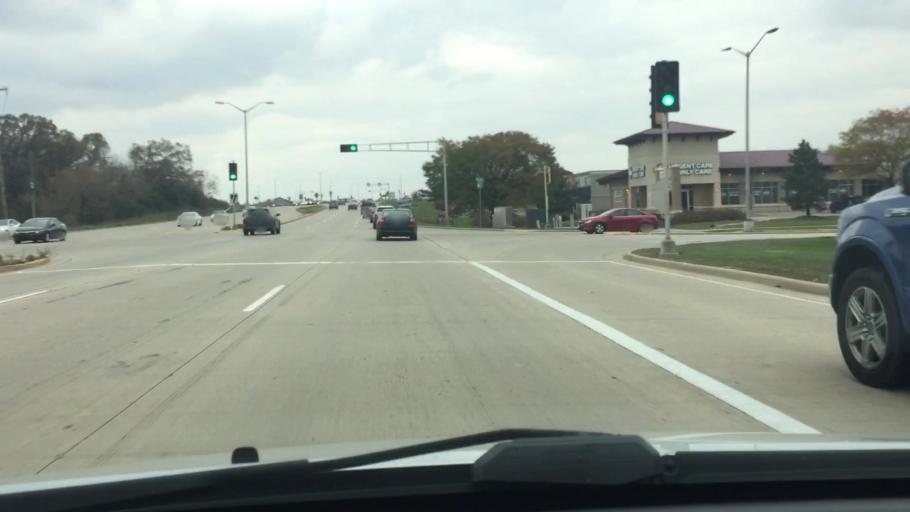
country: US
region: Wisconsin
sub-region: Waukesha County
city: Waukesha
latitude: 43.0171
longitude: -88.2006
